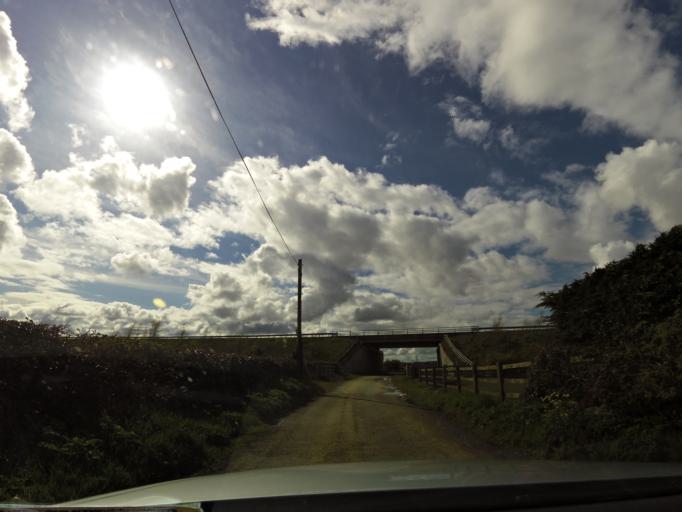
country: IE
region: Leinster
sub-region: Laois
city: Rathdowney
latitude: 52.7772
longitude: -7.5363
